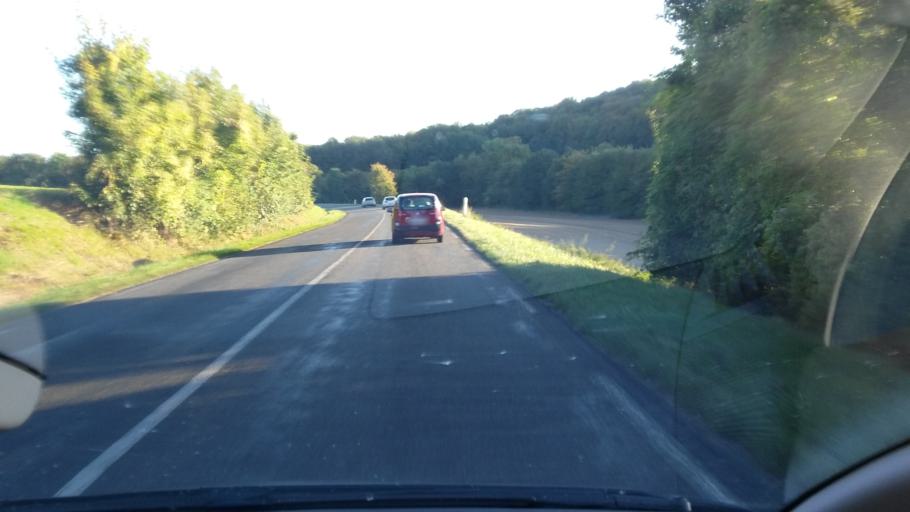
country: FR
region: Champagne-Ardenne
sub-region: Departement de la Marne
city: Verzenay
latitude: 49.1164
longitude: 4.1088
